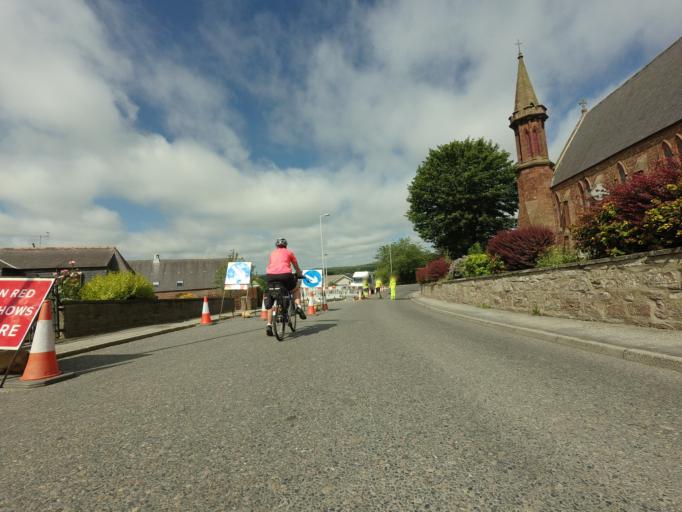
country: GB
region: Scotland
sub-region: Aberdeenshire
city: Turriff
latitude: 57.5390
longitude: -2.4690
